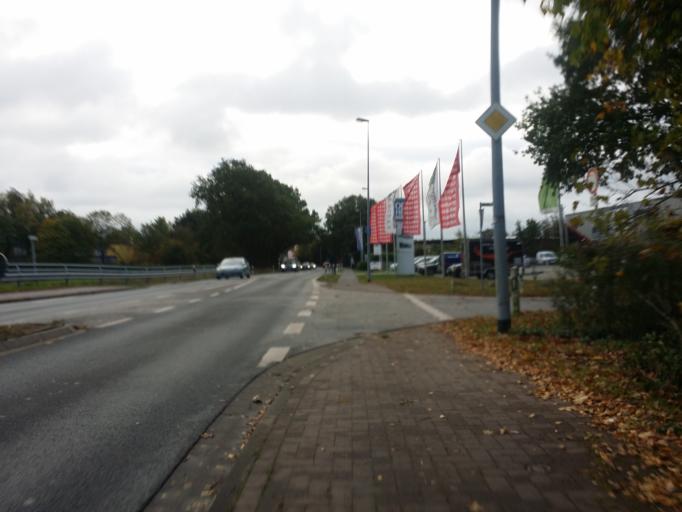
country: DE
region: Lower Saxony
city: Delmenhorst
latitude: 53.0423
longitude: 8.6735
